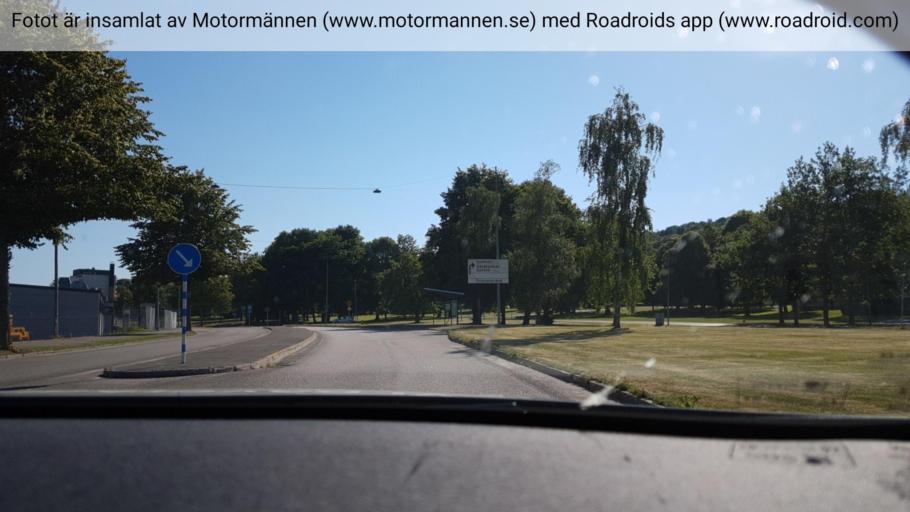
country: SE
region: Vaestra Goetaland
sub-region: Falkopings Kommun
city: Falkoeping
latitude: 58.1884
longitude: 13.5562
